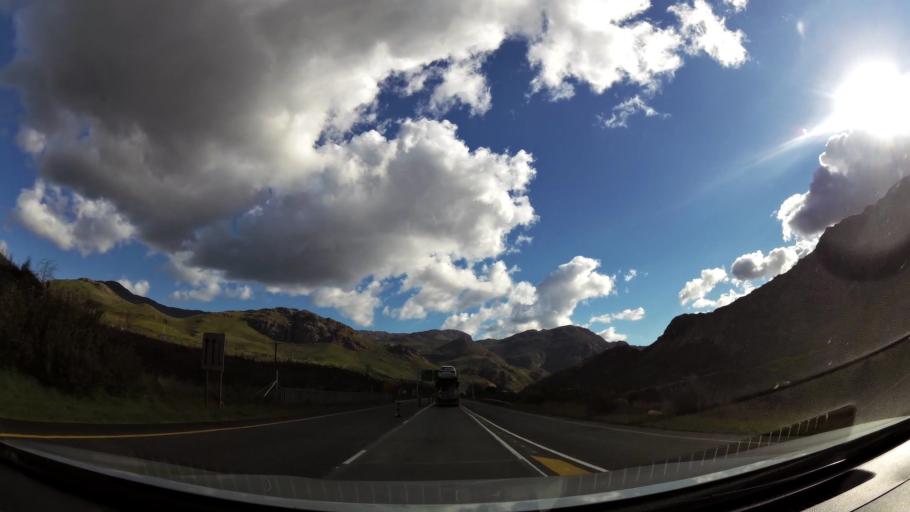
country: ZA
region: Western Cape
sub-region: Cape Winelands District Municipality
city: Paarl
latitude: -33.7269
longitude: 19.1391
